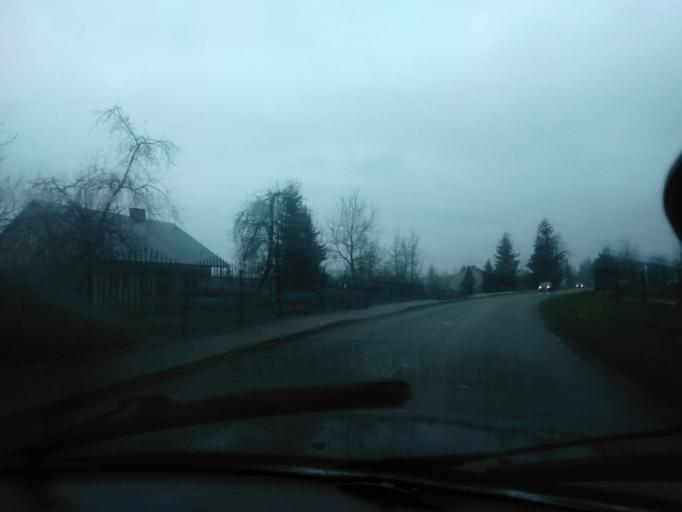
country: PL
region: Subcarpathian Voivodeship
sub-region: Powiat jaroslawski
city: Rokietnica
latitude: 49.9440
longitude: 22.6144
